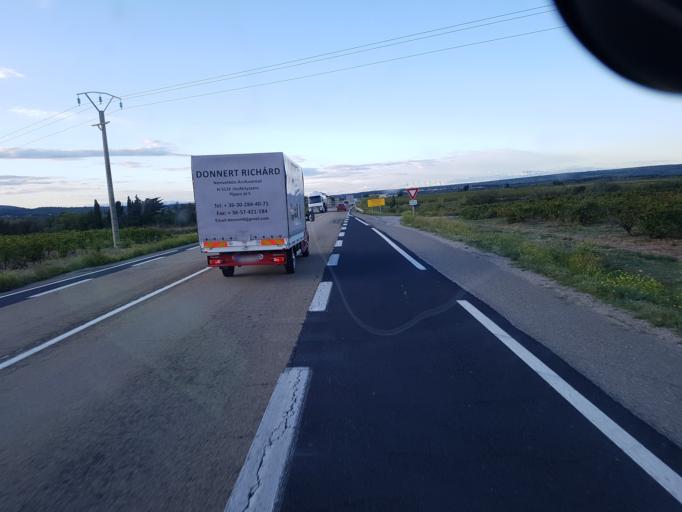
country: FR
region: Languedoc-Roussillon
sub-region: Departement de l'Aude
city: Leucate
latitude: 42.9387
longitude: 2.9906
